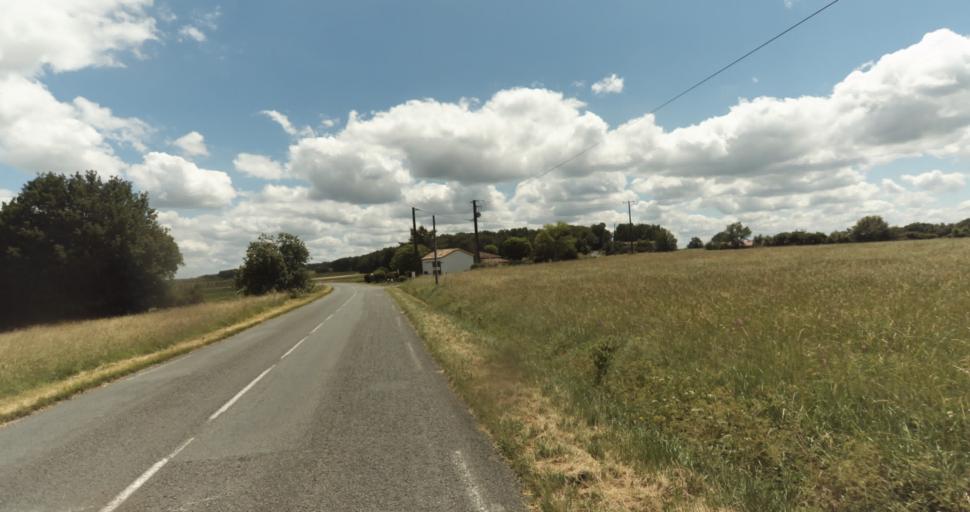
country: FR
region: Aquitaine
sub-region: Departement de la Dordogne
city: Beaumont-du-Perigord
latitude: 44.6976
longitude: 0.8525
